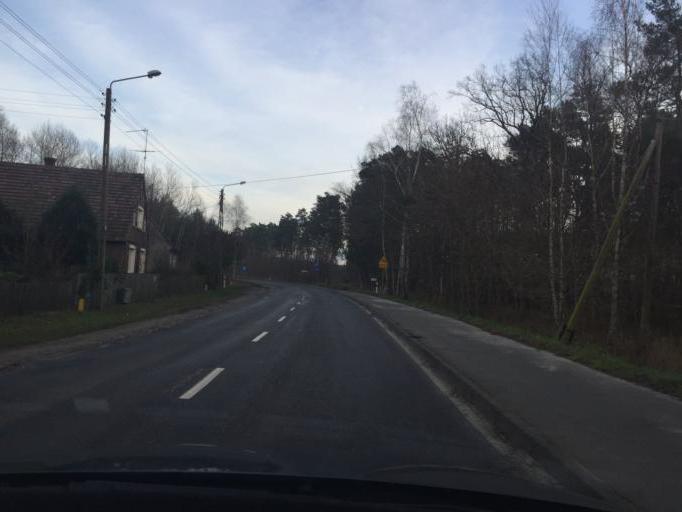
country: PL
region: Lubusz
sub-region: Powiat zarski
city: Lubsko
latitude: 51.7841
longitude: 14.9050
